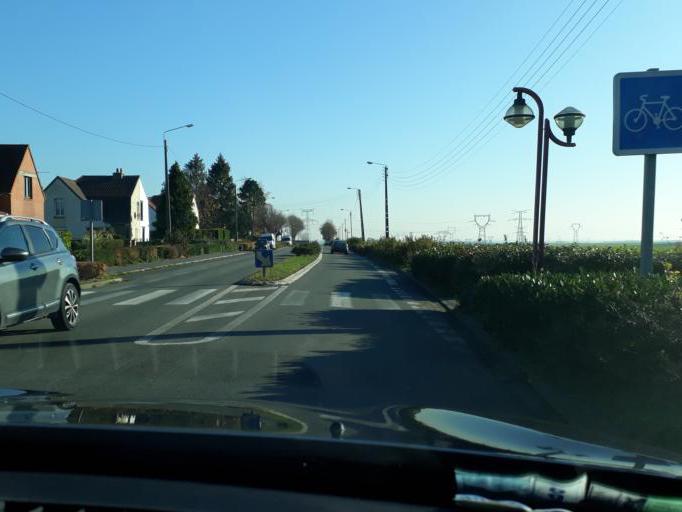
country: FR
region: Nord-Pas-de-Calais
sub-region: Departement du Nord
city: Aniche
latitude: 50.3136
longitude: 3.2696
